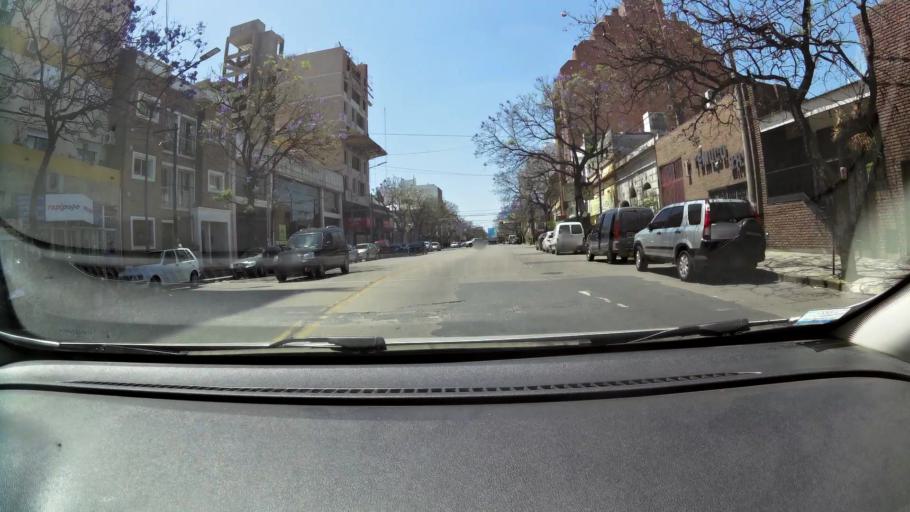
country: AR
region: Cordoba
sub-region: Departamento de Capital
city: Cordoba
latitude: -31.4032
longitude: -64.1986
